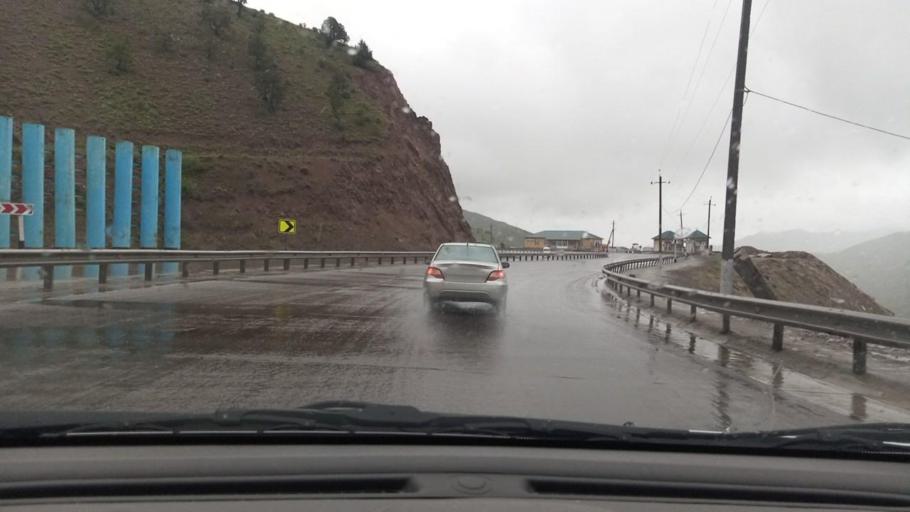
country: UZ
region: Toshkent
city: Angren
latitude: 41.0928
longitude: 70.5316
